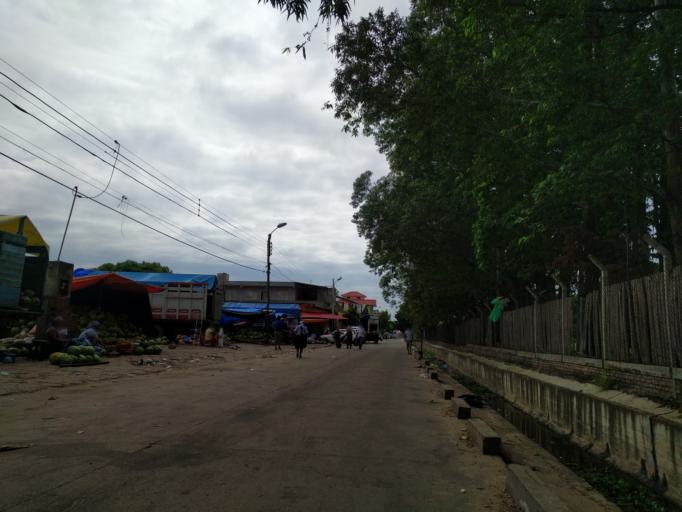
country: BO
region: Santa Cruz
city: Santa Cruz de la Sierra
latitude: -17.7987
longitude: -63.2072
